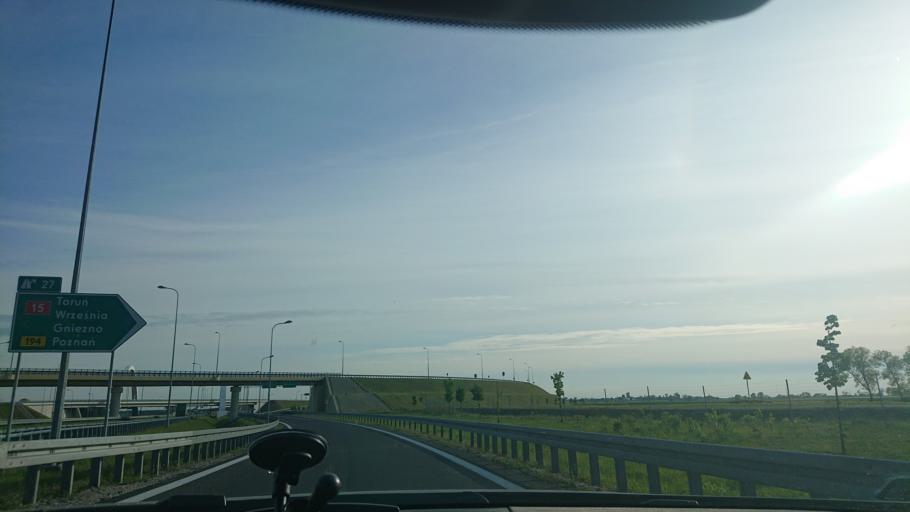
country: PL
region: Greater Poland Voivodeship
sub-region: Powiat gnieznienski
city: Lubowo
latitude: 52.5242
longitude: 17.5084
